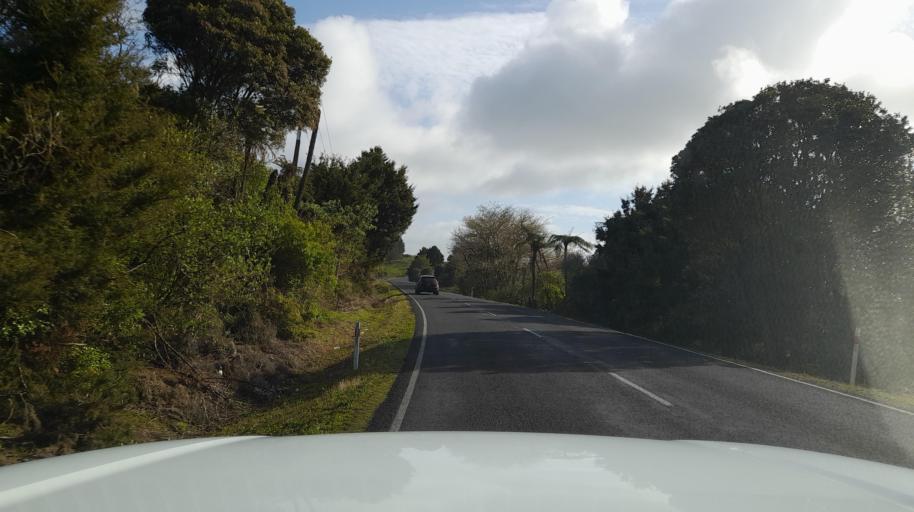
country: NZ
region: Northland
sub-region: Far North District
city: Waimate North
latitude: -35.3785
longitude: 173.8154
